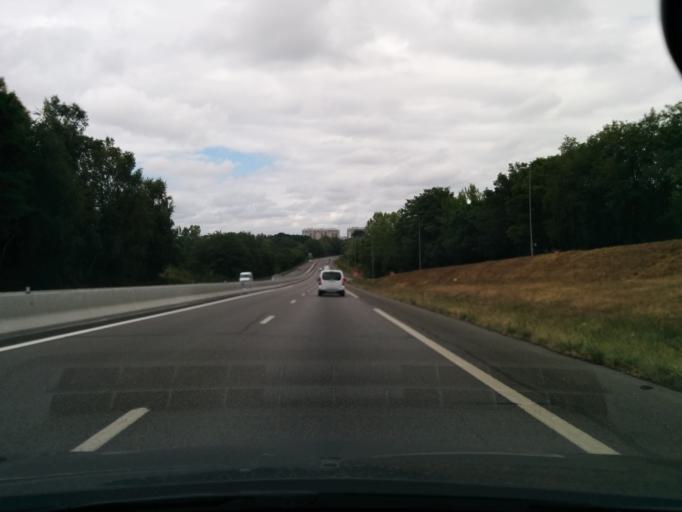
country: FR
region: Limousin
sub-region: Departement de la Haute-Vienne
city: Condat-sur-Vienne
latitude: 45.8191
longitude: 1.2924
